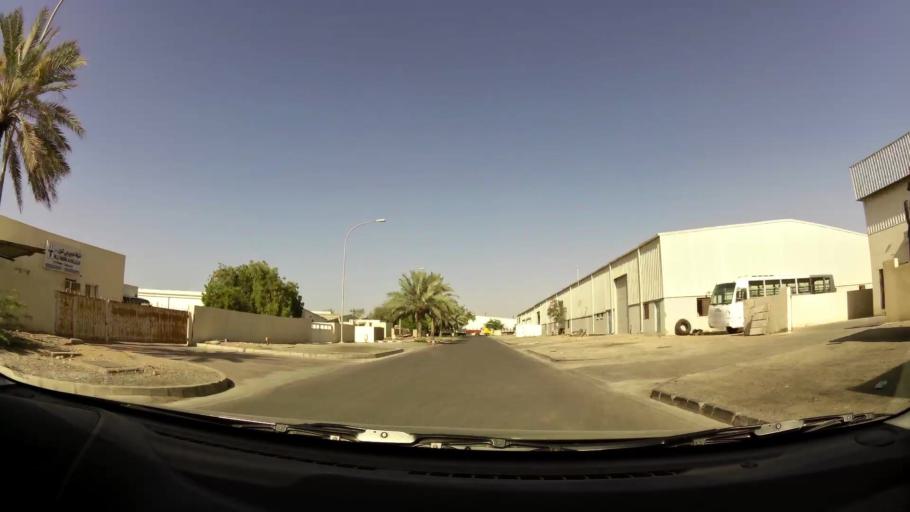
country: OM
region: Muhafazat Masqat
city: As Sib al Jadidah
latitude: 23.5555
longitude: 58.2059
